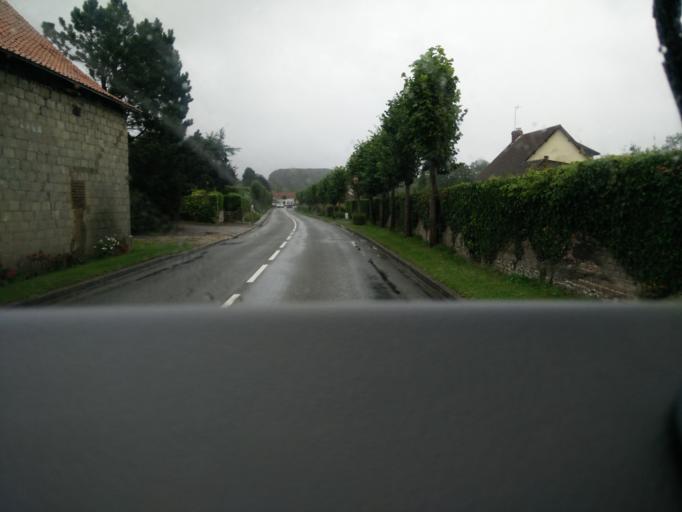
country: FR
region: Picardie
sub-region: Departement de la Somme
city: Nouvion
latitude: 50.2781
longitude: 1.7643
